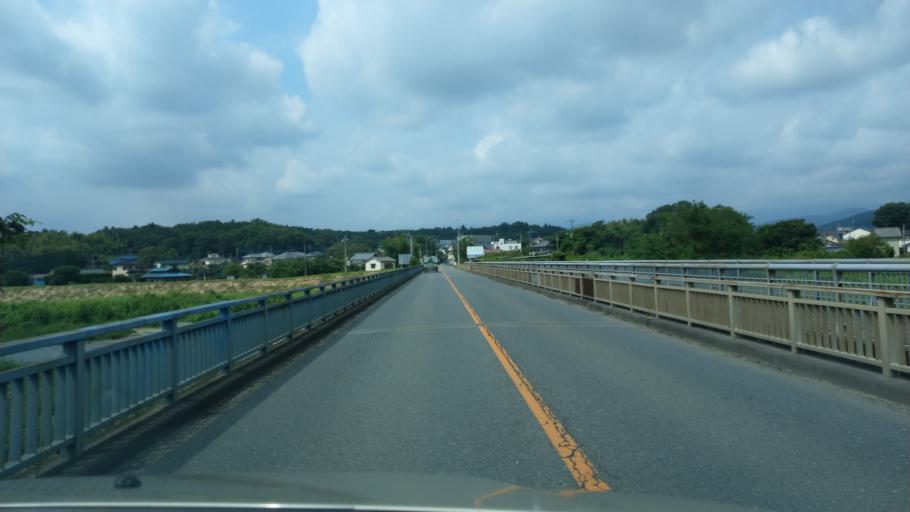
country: JP
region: Saitama
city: Ogawa
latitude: 36.0301
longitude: 139.3360
